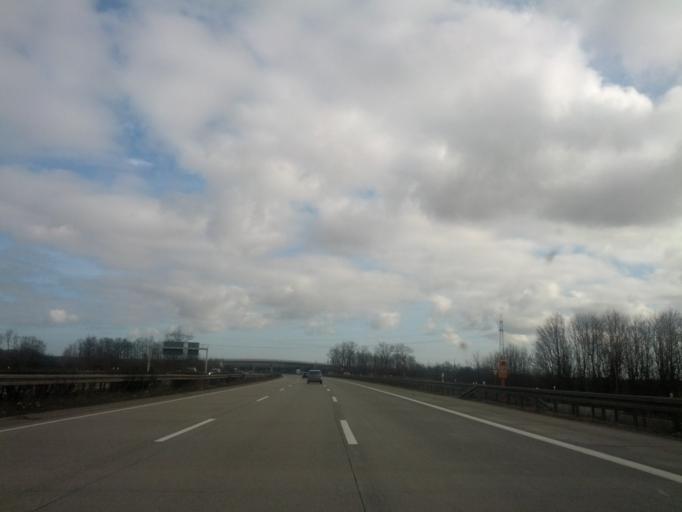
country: DE
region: Lower Saxony
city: Lehrte
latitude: 52.3594
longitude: 9.8873
